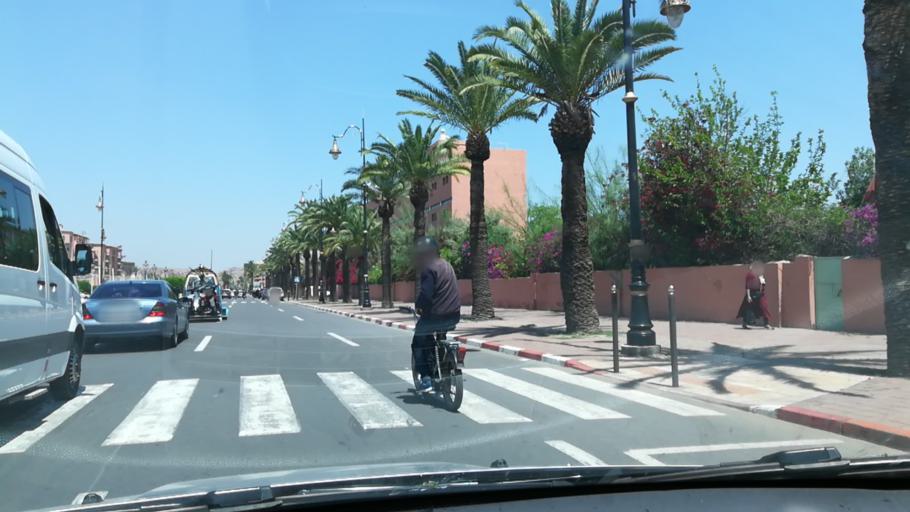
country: MA
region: Marrakech-Tensift-Al Haouz
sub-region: Marrakech
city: Marrakesh
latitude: 31.6269
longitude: -8.0138
